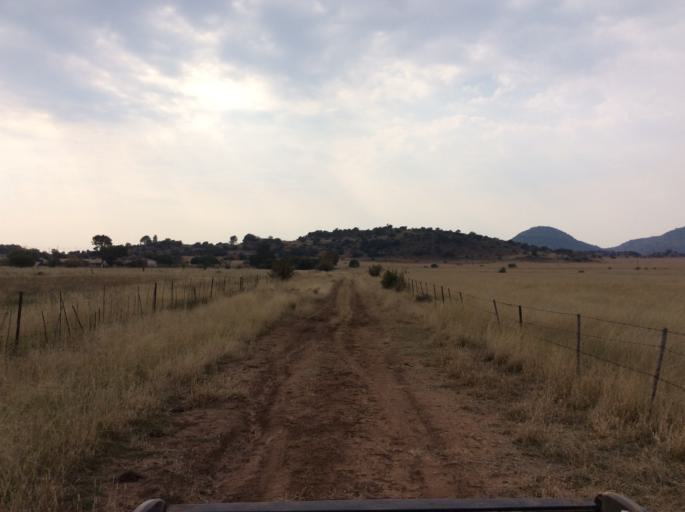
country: LS
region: Mafeteng
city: Mafeteng
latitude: -29.9911
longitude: 27.0178
